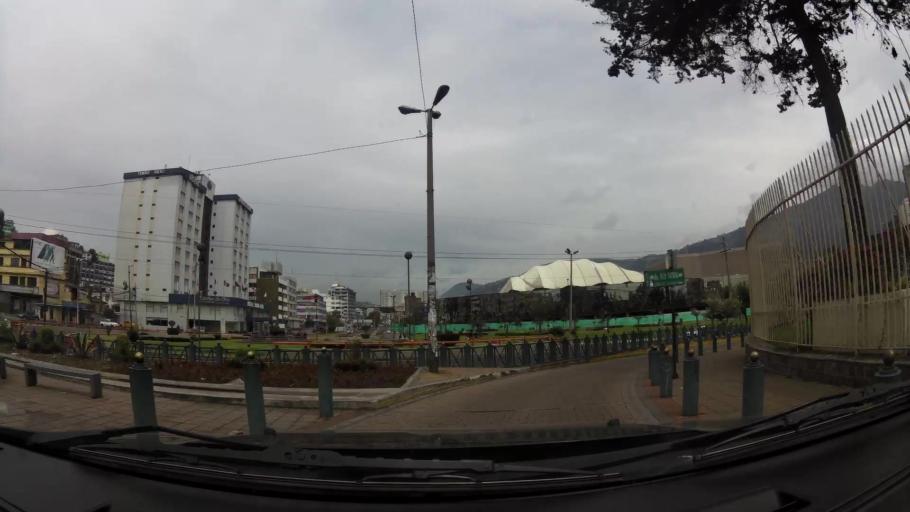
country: EC
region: Pichincha
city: Quito
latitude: -0.2101
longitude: -78.4936
